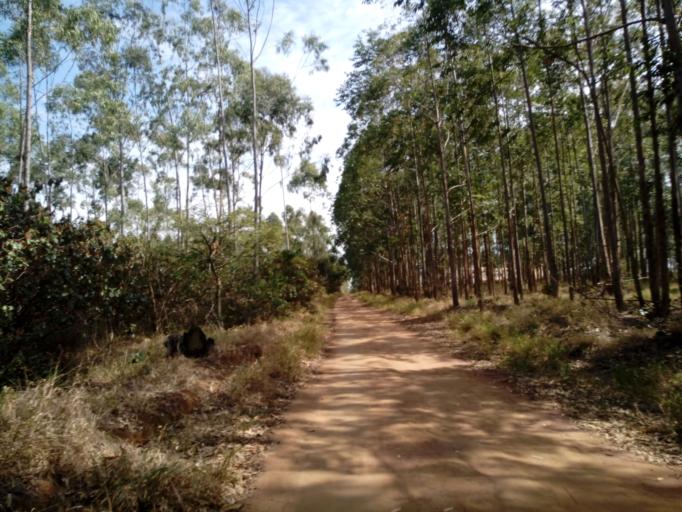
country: BR
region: Sao Paulo
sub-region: Sao Carlos
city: Sao Carlos
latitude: -21.9725
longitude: -47.8770
